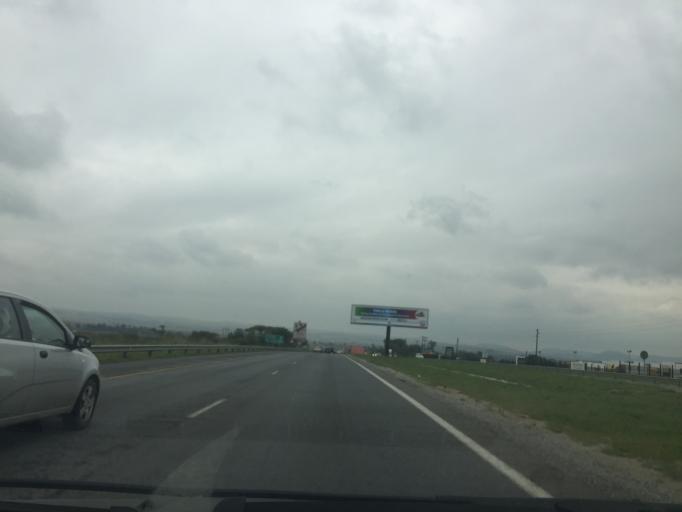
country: ZA
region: Gauteng
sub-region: City of Johannesburg Metropolitan Municipality
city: Diepsloot
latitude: -25.9465
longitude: 27.9102
